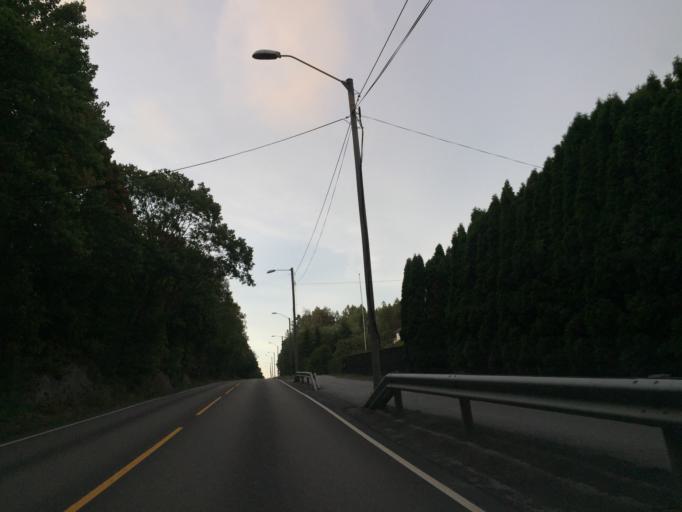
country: NO
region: Ostfold
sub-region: Fredrikstad
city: Fredrikstad
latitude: 59.1844
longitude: 10.9279
